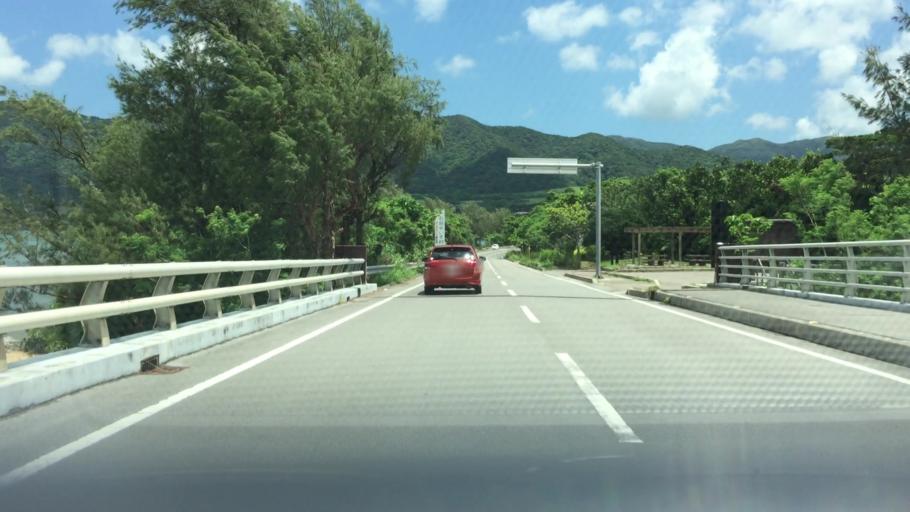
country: JP
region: Okinawa
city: Ishigaki
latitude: 24.4027
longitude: 124.1412
